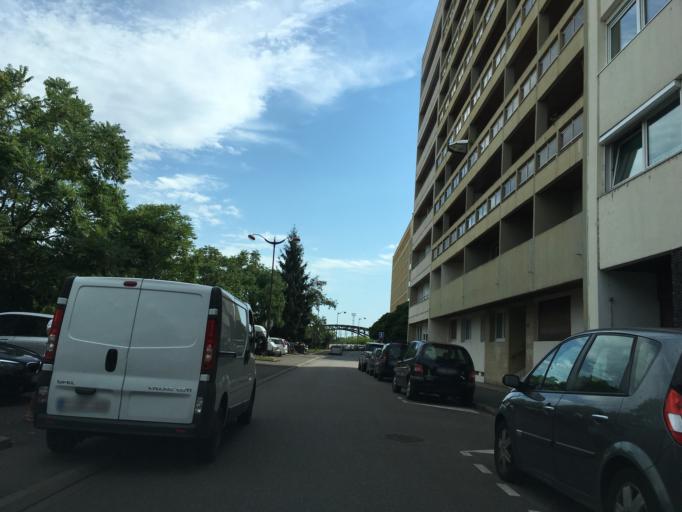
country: FR
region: Lorraine
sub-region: Departement de la Moselle
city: Metz
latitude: 49.1037
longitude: 6.1691
